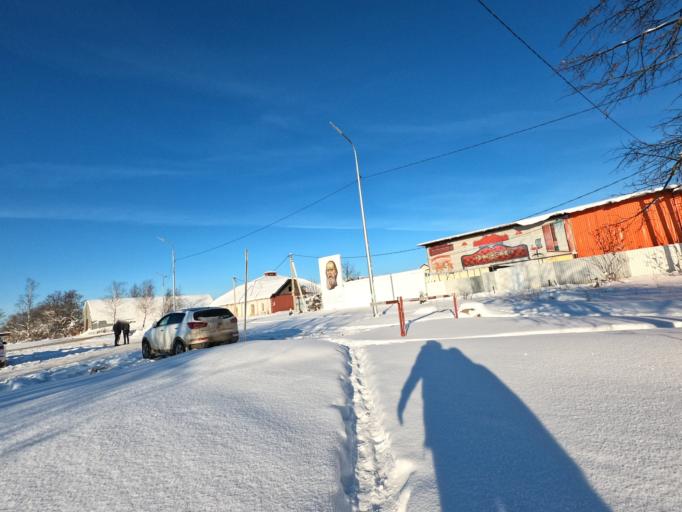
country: RU
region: Moskovskaya
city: Taldom
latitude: 56.7231
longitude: 37.5267
